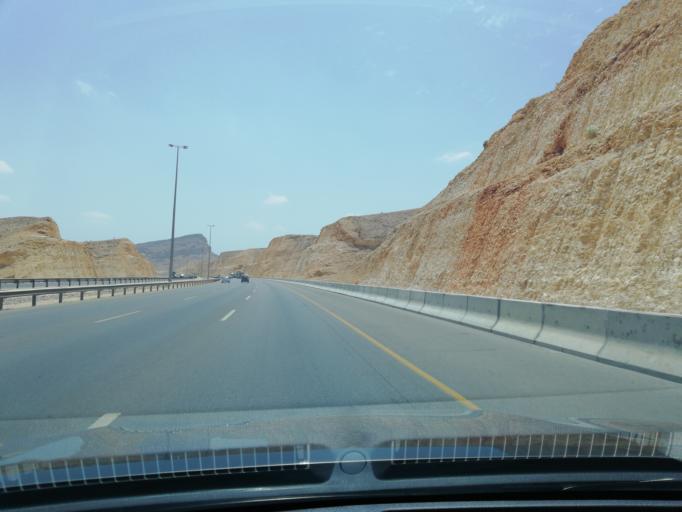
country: OM
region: Muhafazat Masqat
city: As Sib al Jadidah
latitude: 23.5453
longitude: 58.2401
